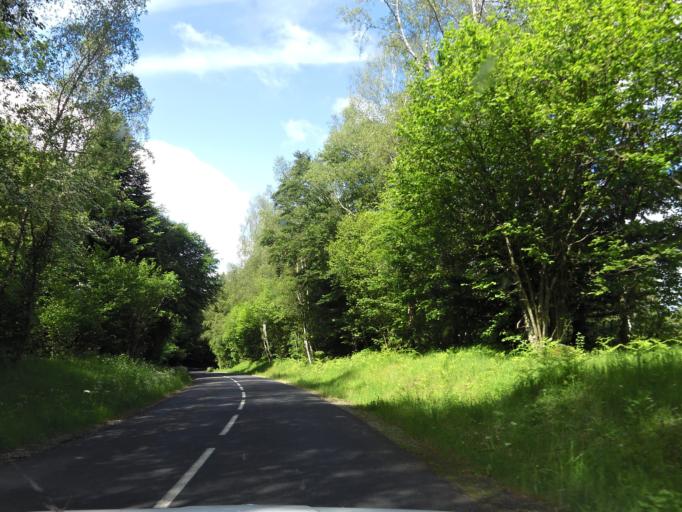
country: FR
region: Auvergne
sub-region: Departement du Puy-de-Dome
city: Orcines
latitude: 45.7651
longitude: 2.9264
